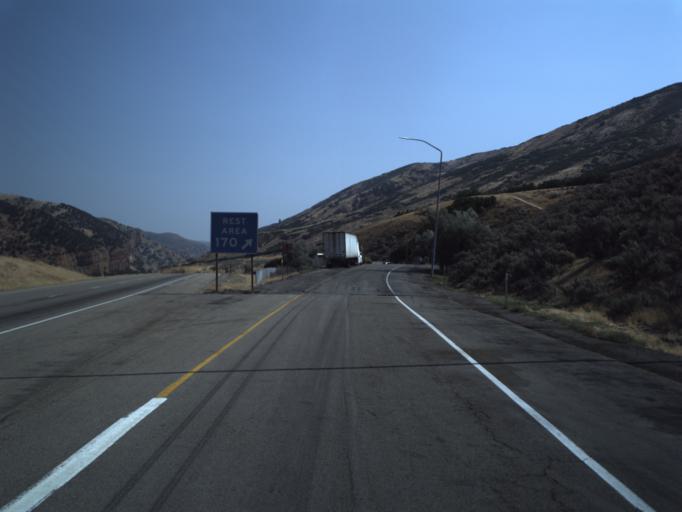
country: US
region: Utah
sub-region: Summit County
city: Coalville
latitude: 40.9887
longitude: -111.4051
